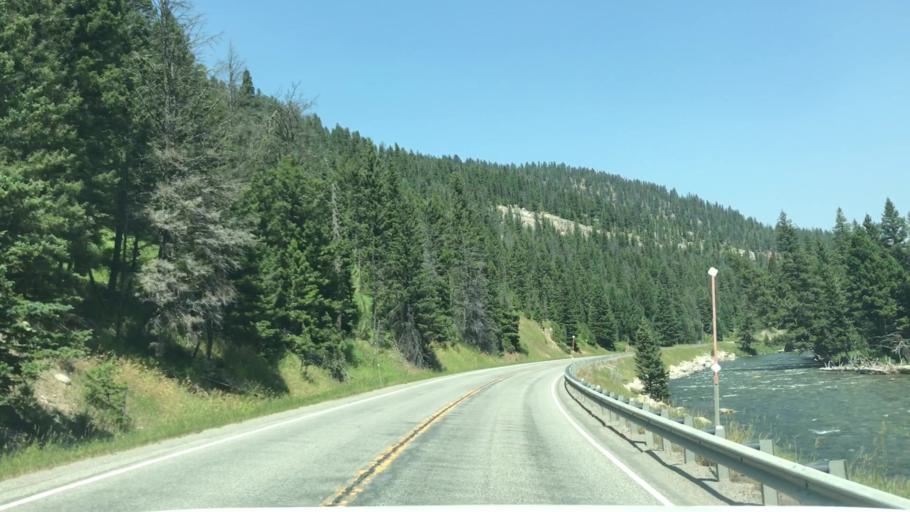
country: US
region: Montana
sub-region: Gallatin County
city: Big Sky
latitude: 45.1601
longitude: -111.2489
